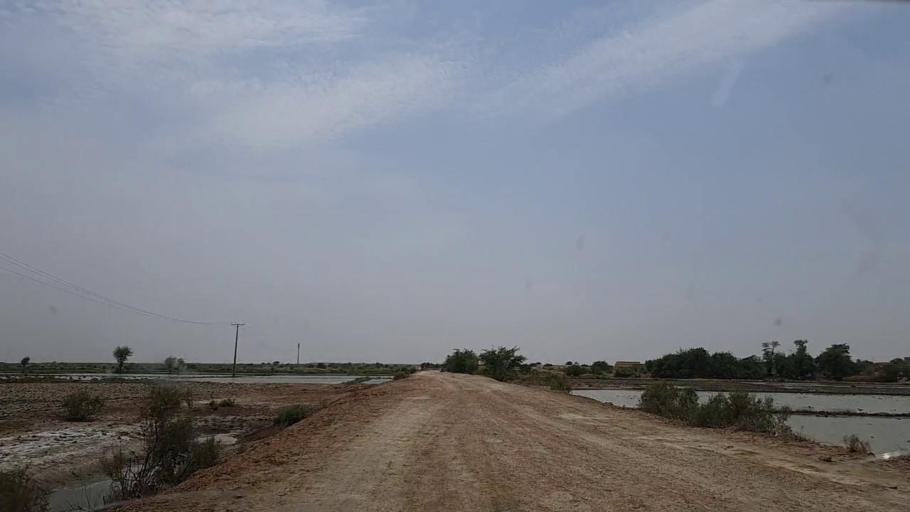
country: PK
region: Sindh
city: Phulji
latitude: 26.8760
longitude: 67.6558
